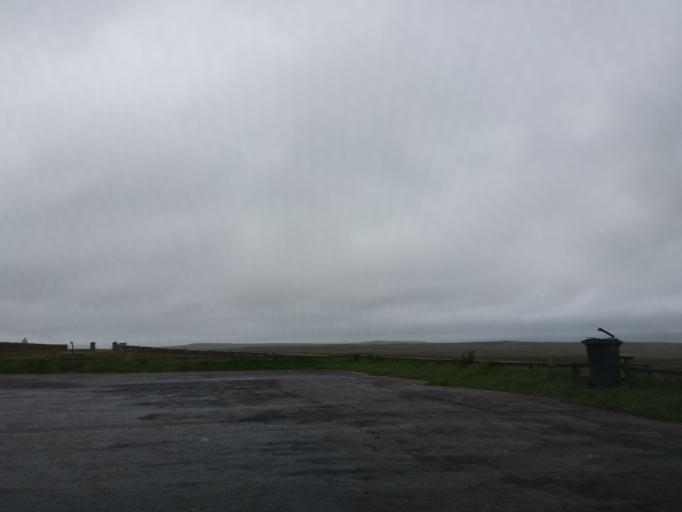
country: GB
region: Scotland
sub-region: Highland
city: Thurso
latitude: 58.6705
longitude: -3.3766
